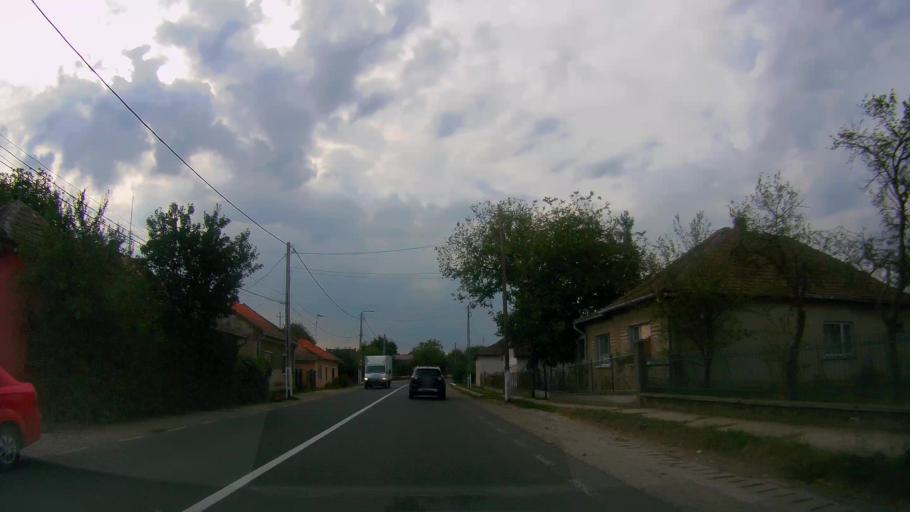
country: RO
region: Satu Mare
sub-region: Oras Ardud
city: Ardud
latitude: 47.5866
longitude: 22.8849
